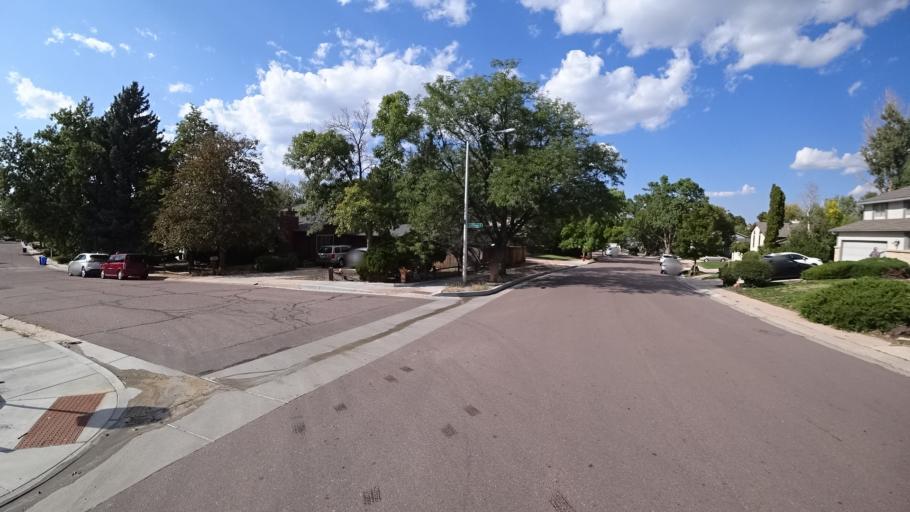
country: US
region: Colorado
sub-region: El Paso County
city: Cimarron Hills
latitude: 38.8748
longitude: -104.7336
